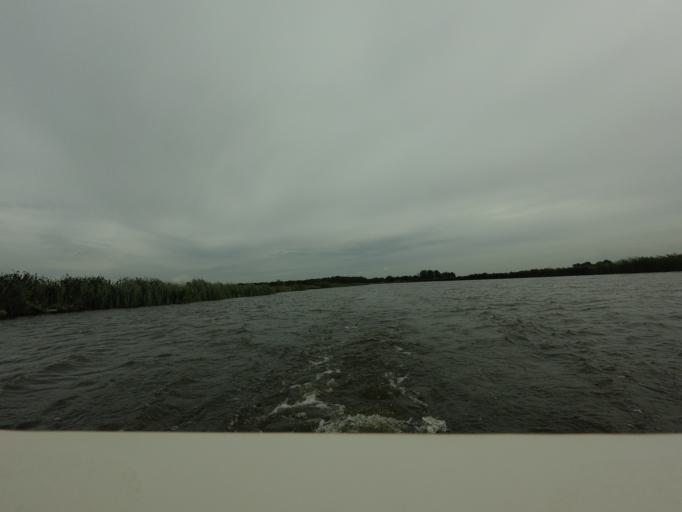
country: NL
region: Friesland
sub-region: Gemeente Boarnsterhim
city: Grou
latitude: 53.1112
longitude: 5.8731
